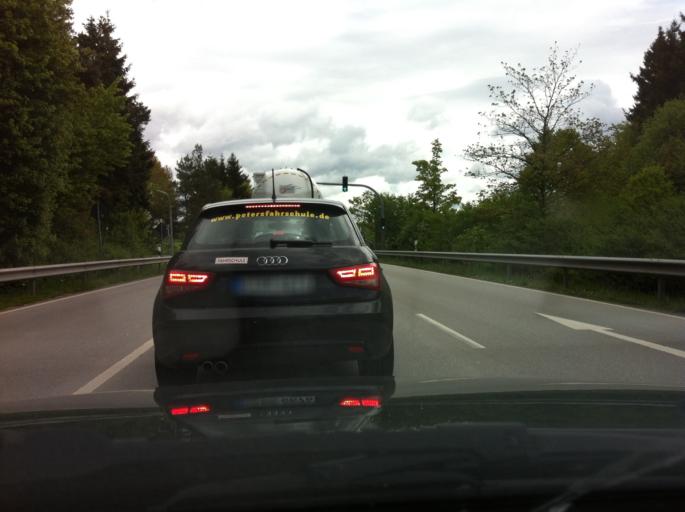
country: DE
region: Bavaria
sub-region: Upper Bavaria
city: Brunnthal
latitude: 47.9786
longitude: 11.6866
